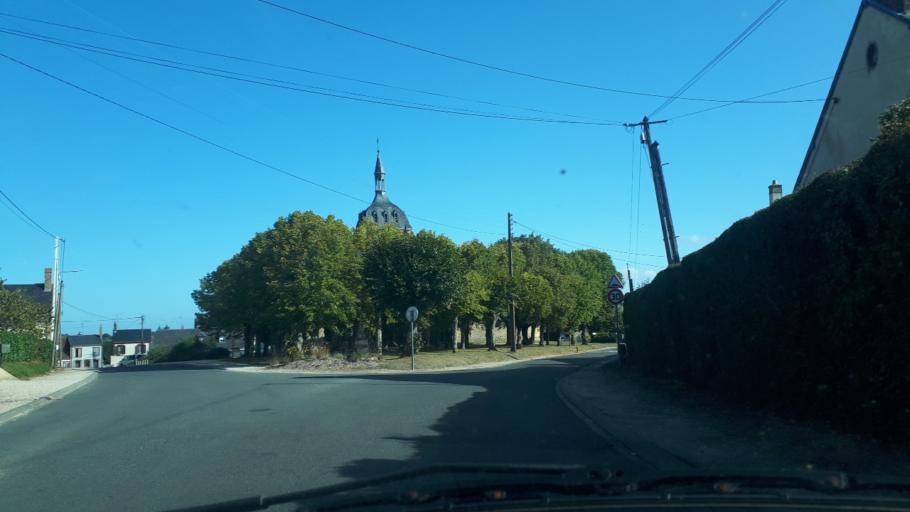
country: FR
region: Centre
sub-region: Departement du Loir-et-Cher
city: Mondoubleau
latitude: 47.9969
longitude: 0.9271
